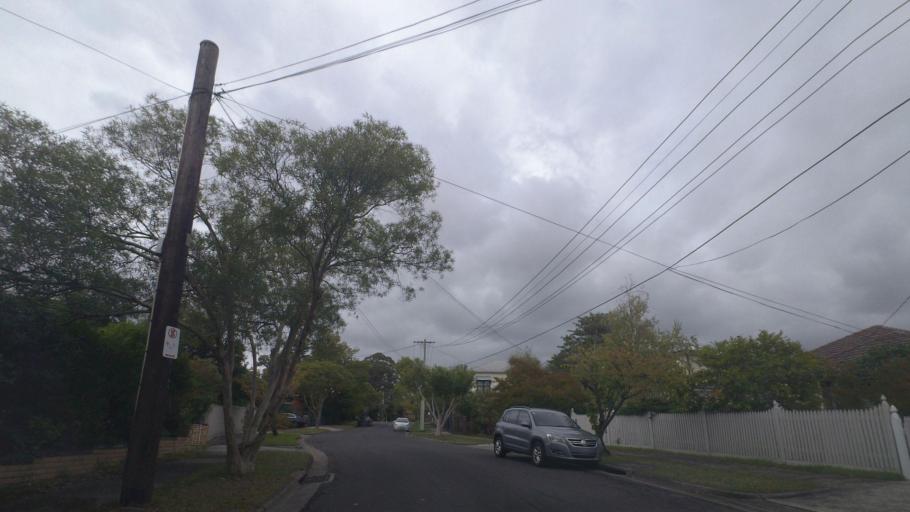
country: AU
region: Victoria
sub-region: Whitehorse
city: Nunawading
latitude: -37.8238
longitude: 145.1706
